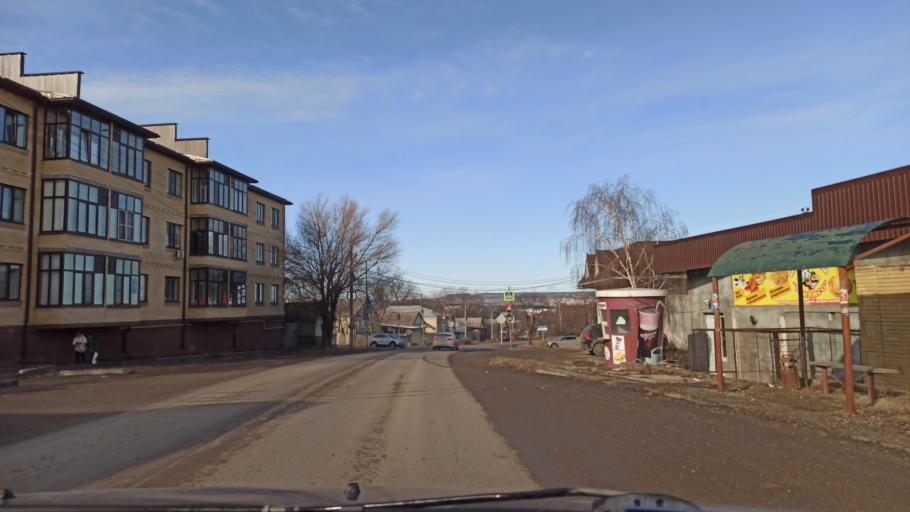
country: RU
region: Stavropol'skiy
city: Yessentukskaya
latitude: 44.0238
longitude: 42.8697
